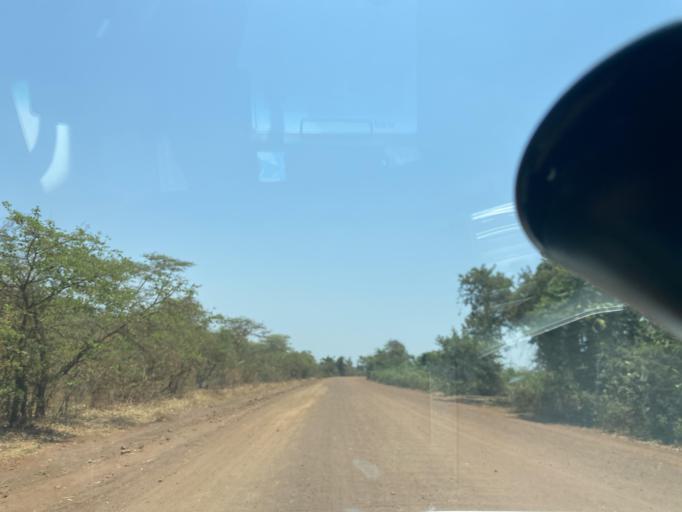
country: ZM
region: Southern
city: Nakambala
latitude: -15.4921
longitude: 27.9036
